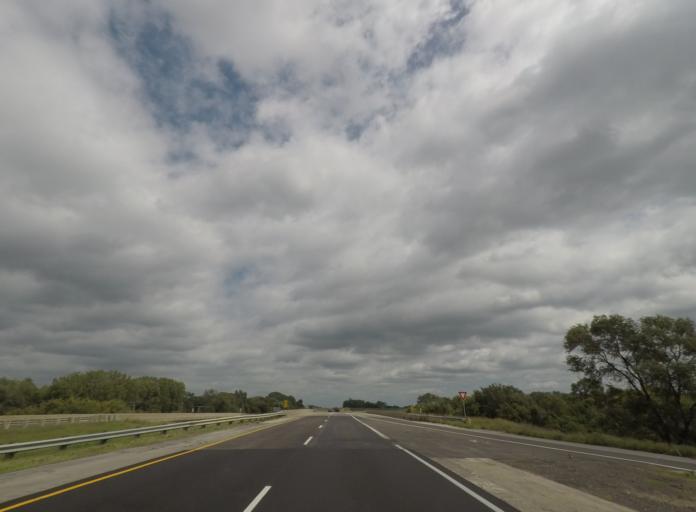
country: US
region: Iowa
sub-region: Linn County
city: Ely
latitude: 41.9265
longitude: -91.6334
